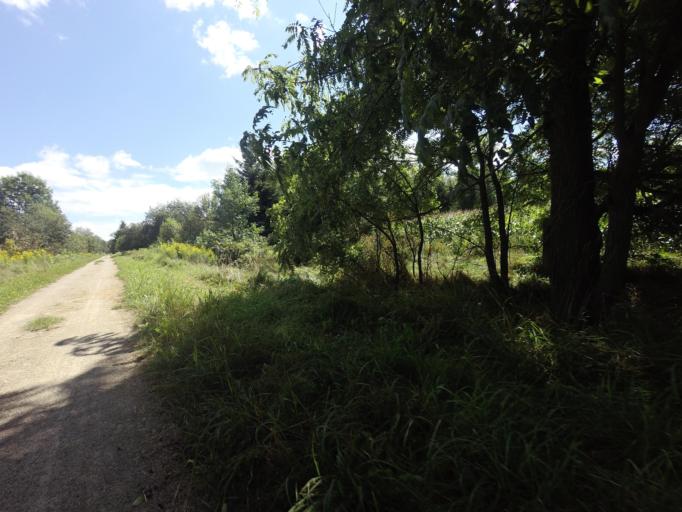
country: CA
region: Ontario
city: Orangeville
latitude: 43.7923
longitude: -80.2982
